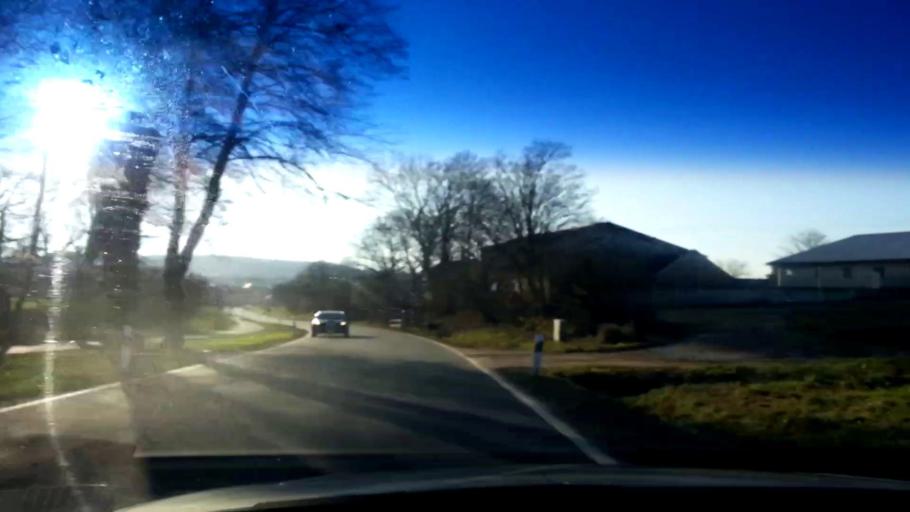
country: DE
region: Bavaria
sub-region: Upper Franconia
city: Litzendorf
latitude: 49.9150
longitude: 10.9959
